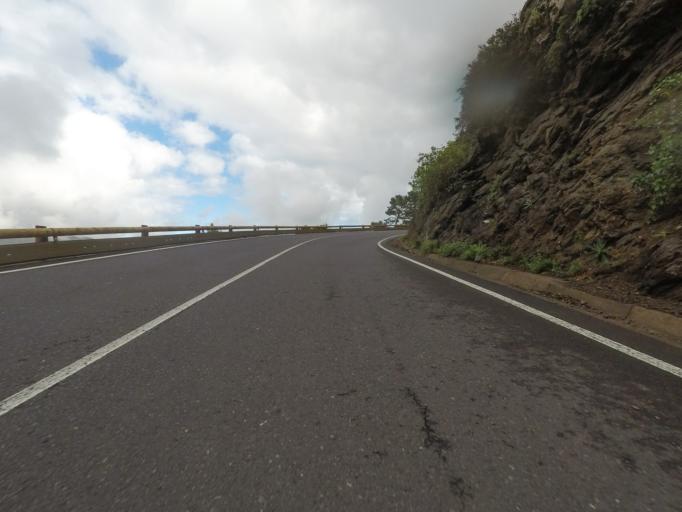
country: ES
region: Canary Islands
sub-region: Provincia de Santa Cruz de Tenerife
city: Hermigua
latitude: 28.1358
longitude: -17.1993
